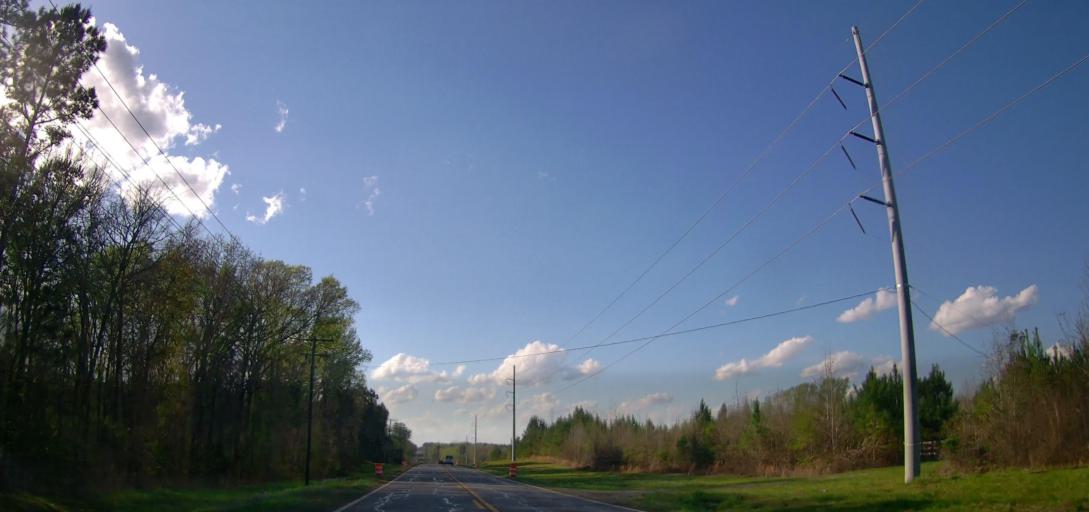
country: US
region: Georgia
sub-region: Baldwin County
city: Milledgeville
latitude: 33.1425
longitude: -83.3337
